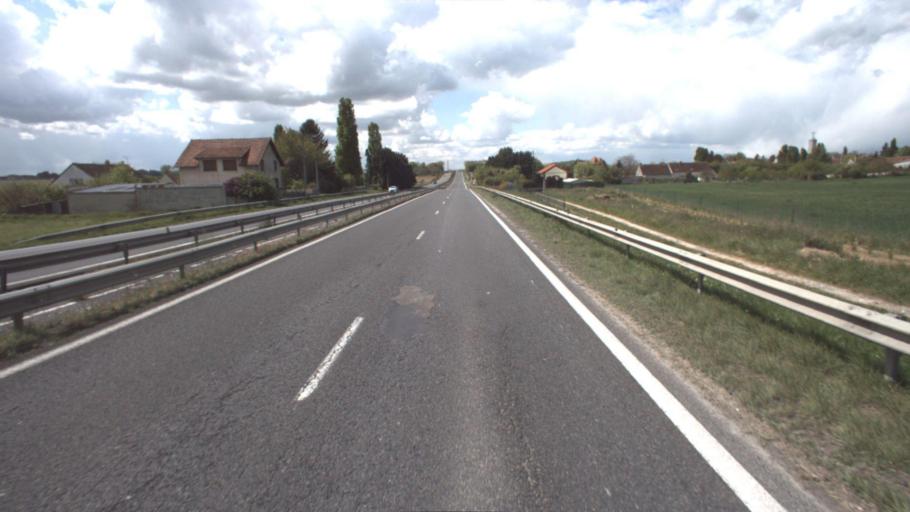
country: FR
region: Ile-de-France
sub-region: Departement de Seine-et-Marne
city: Jouy-le-Chatel
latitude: 48.6845
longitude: 3.0839
